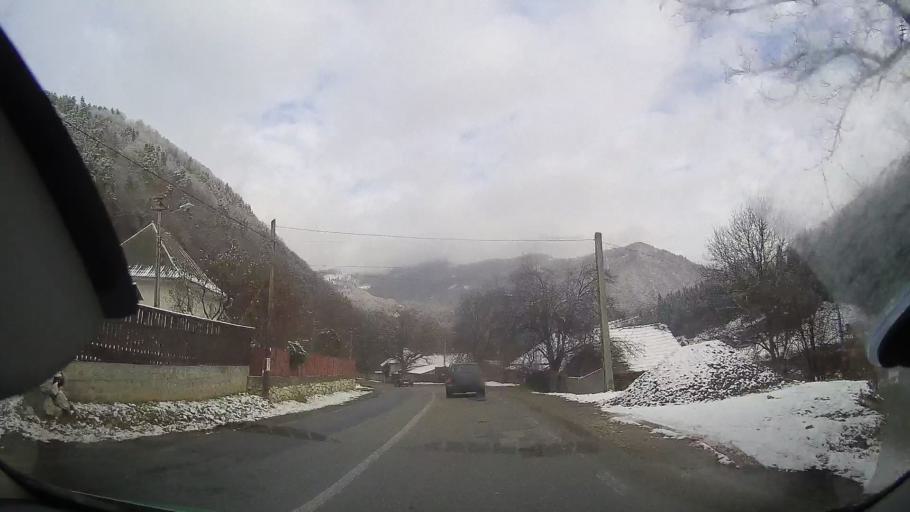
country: RO
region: Alba
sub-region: Oras Baia de Aries
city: Baia de Aries
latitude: 46.4003
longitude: 23.3211
